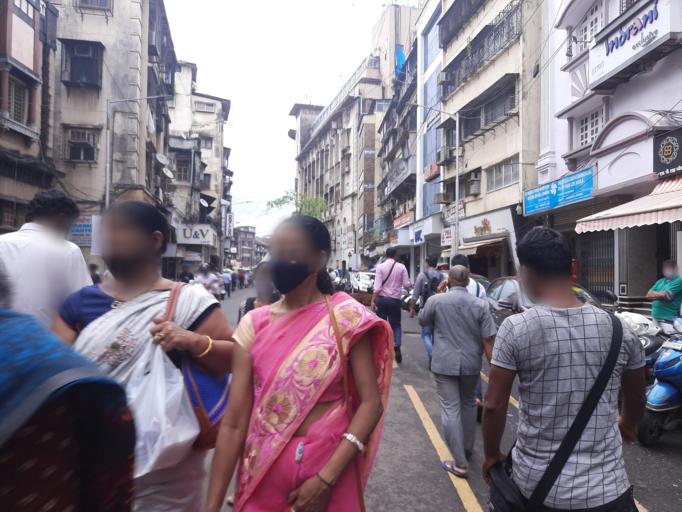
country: IN
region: Maharashtra
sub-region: Raigarh
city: Uran
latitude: 18.9514
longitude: 72.8294
